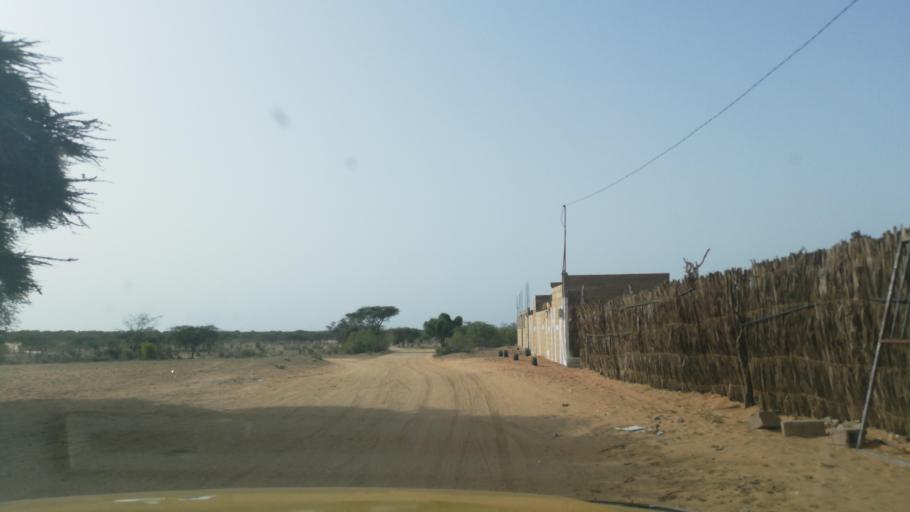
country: SN
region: Saint-Louis
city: Saint-Louis
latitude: 16.0569
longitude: -16.3323
